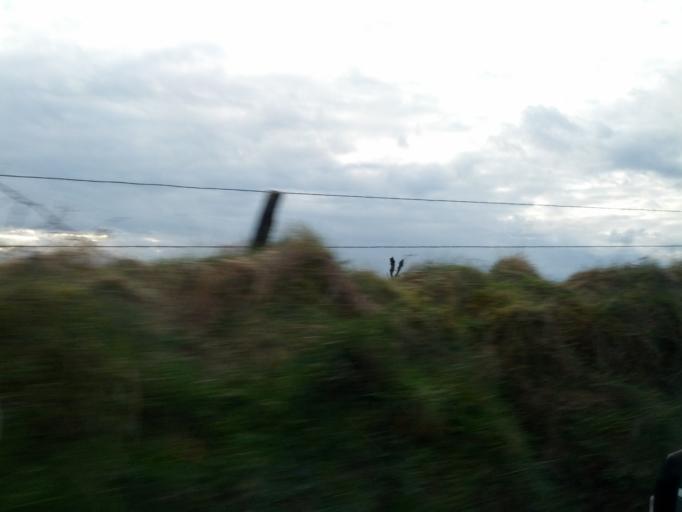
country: IE
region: Connaught
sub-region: County Galway
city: Athenry
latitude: 53.3851
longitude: -8.7243
